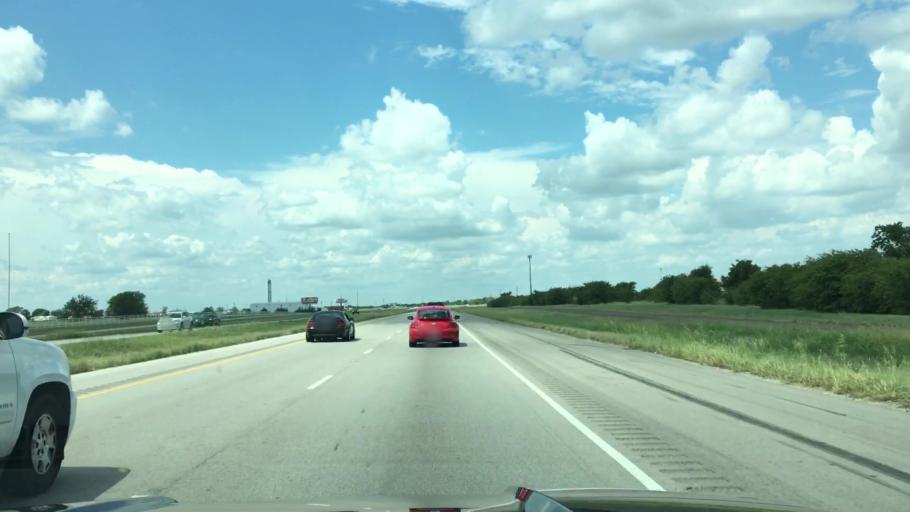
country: US
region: Texas
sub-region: Wise County
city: Rhome
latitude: 33.0320
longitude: -97.4474
